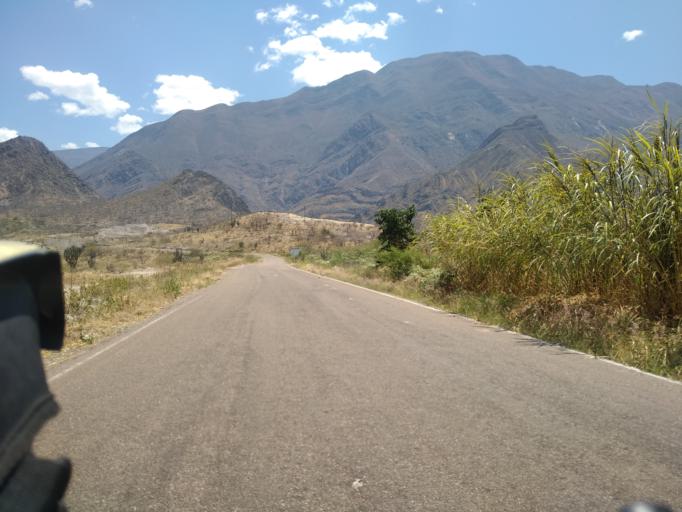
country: PE
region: Amazonas
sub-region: Provincia de Chachapoyas
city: Balsas
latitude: -6.8472
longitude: -78.0353
